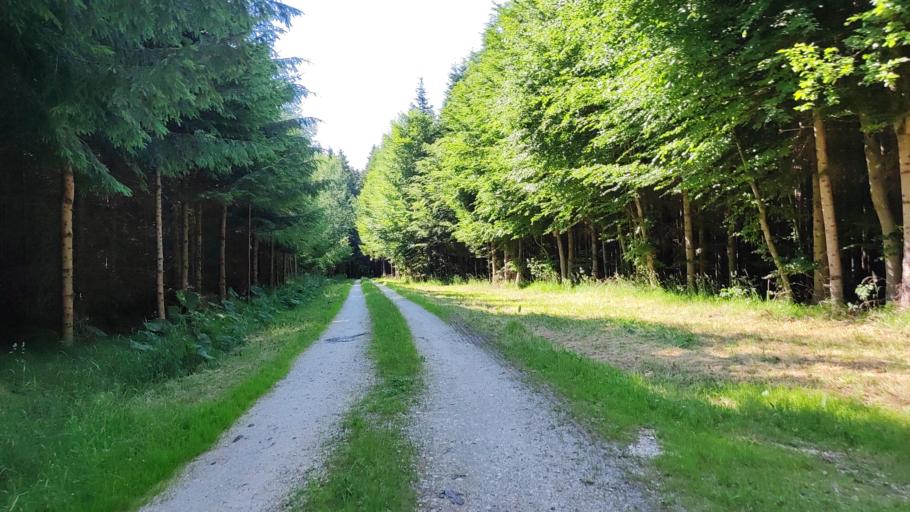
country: DE
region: Bavaria
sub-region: Swabia
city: Burtenbach
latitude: 48.3669
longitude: 10.4998
